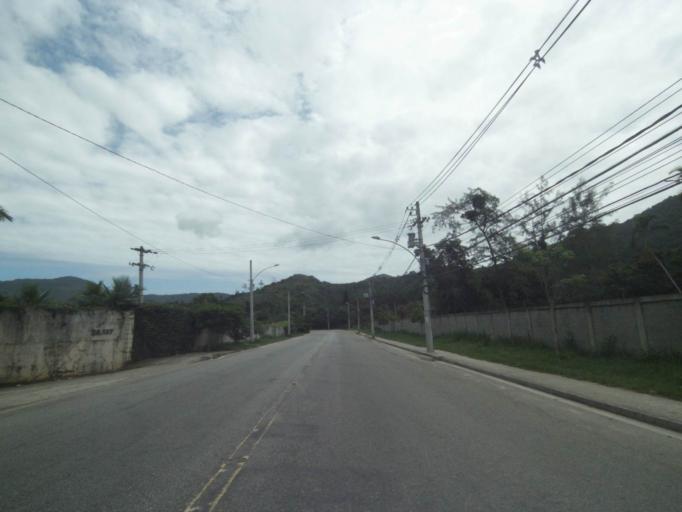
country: BR
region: Rio de Janeiro
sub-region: Nilopolis
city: Nilopolis
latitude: -23.0012
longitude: -43.5094
